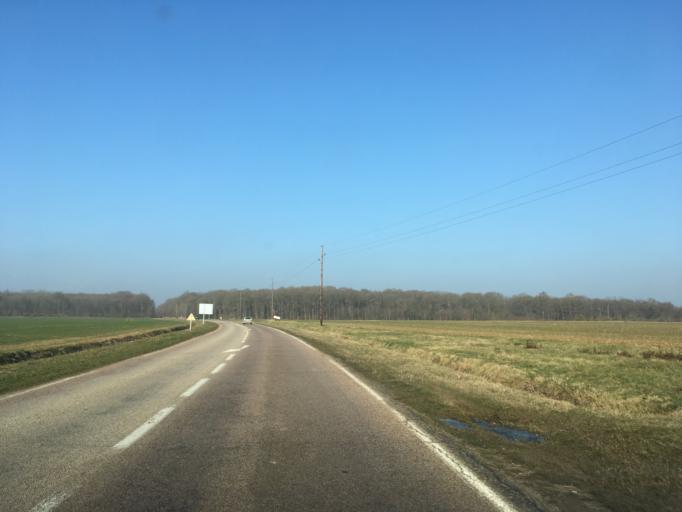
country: FR
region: Haute-Normandie
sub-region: Departement de l'Eure
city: Saint-Marcel
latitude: 49.0798
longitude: 1.4471
